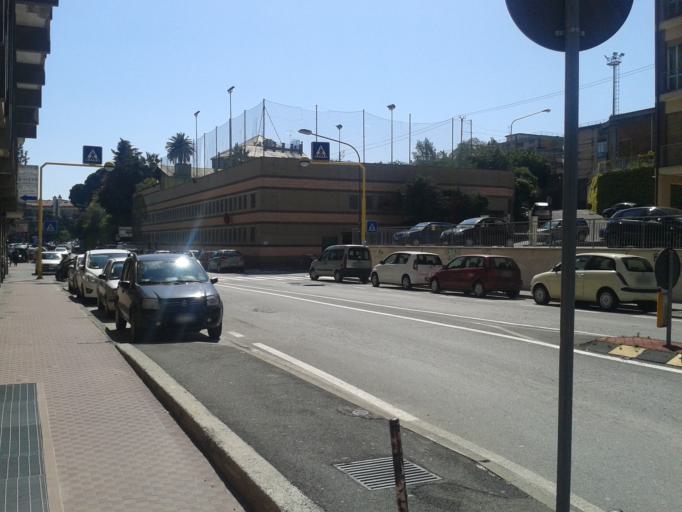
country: IT
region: Liguria
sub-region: Provincia di Savona
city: Savona
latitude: 44.3042
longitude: 8.4707
